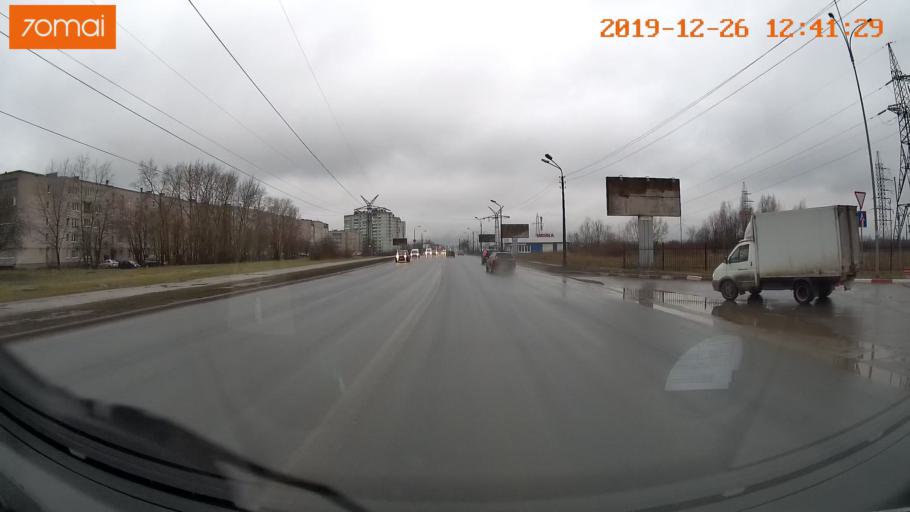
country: RU
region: Vologda
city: Tonshalovo
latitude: 59.1493
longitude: 37.9601
